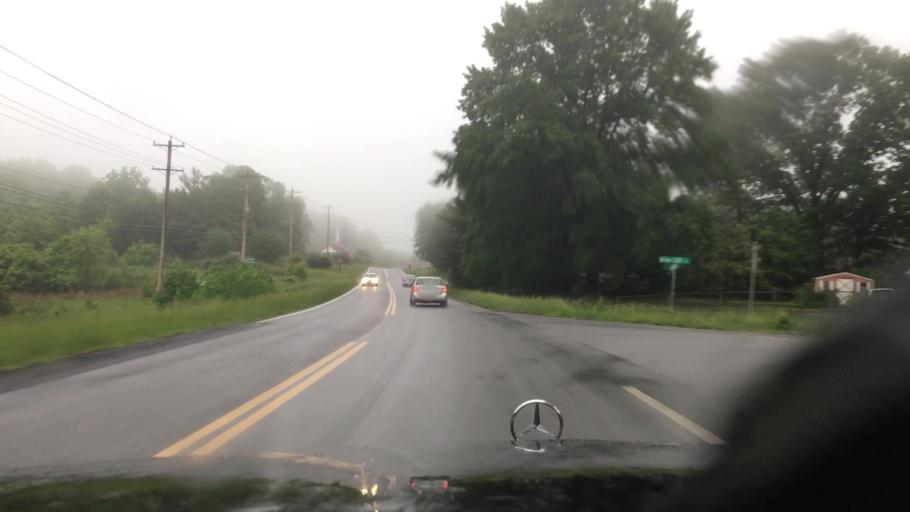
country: US
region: Virginia
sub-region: Campbell County
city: Timberlake
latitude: 37.3242
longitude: -79.2289
